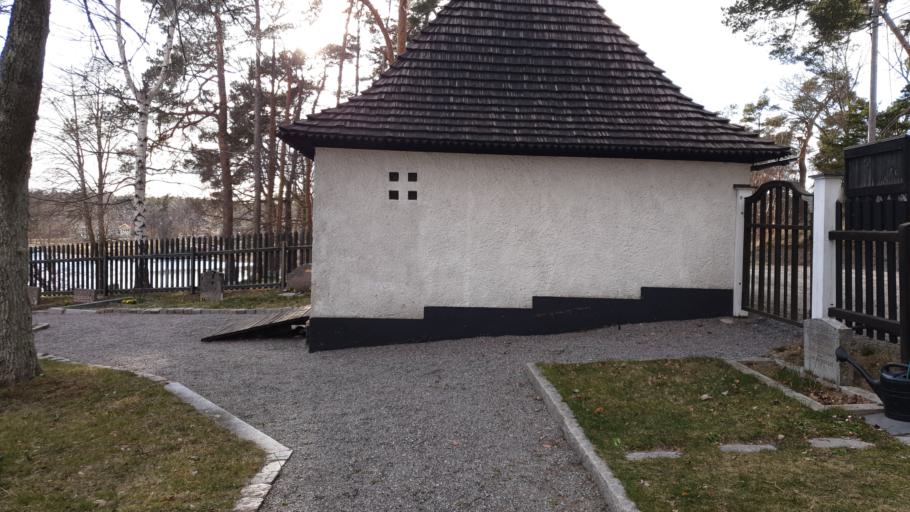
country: SE
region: Stockholm
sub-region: Varmdo Kommun
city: Holo
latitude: 59.3056
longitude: 18.6895
